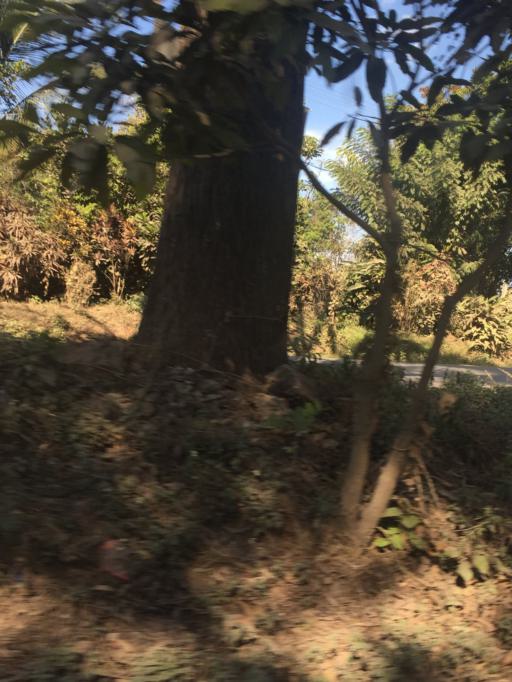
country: MM
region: Mandalay
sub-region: Pyin Oo Lwin District
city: Pyin Oo Lwin
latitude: 21.9516
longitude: 96.4009
